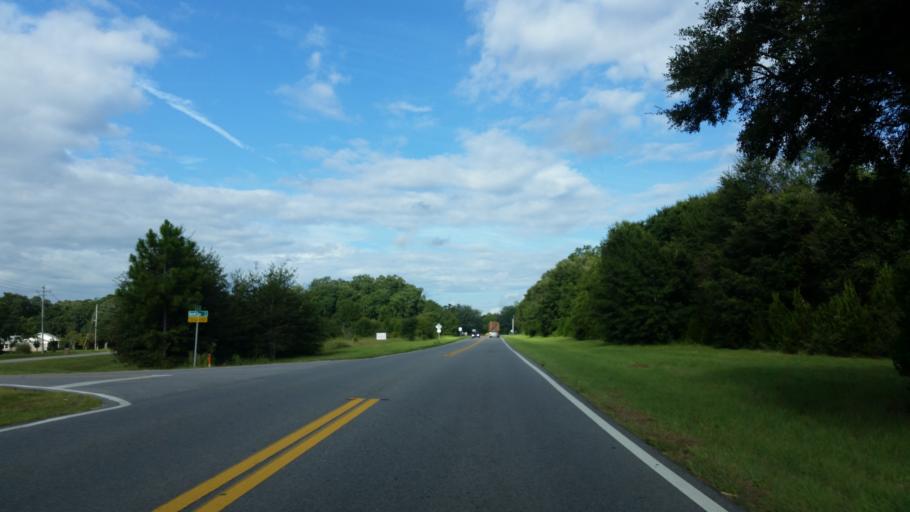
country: US
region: Florida
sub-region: Santa Rosa County
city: Wallace
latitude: 30.6447
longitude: -87.1759
